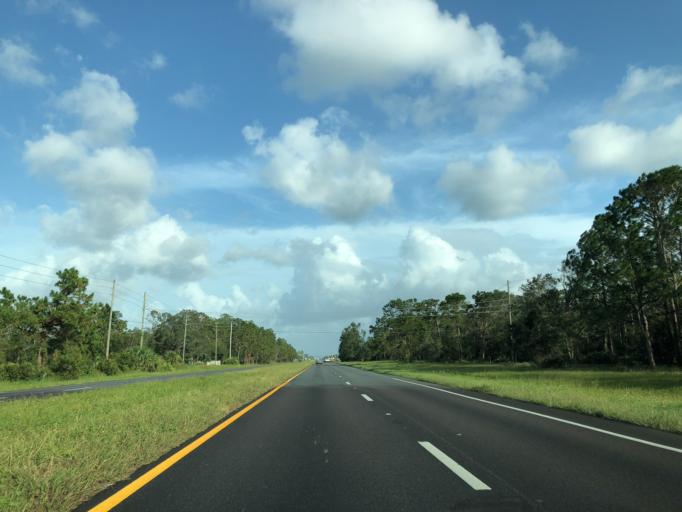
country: US
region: Florida
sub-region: Orange County
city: Bithlo
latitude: 28.5635
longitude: -81.1387
